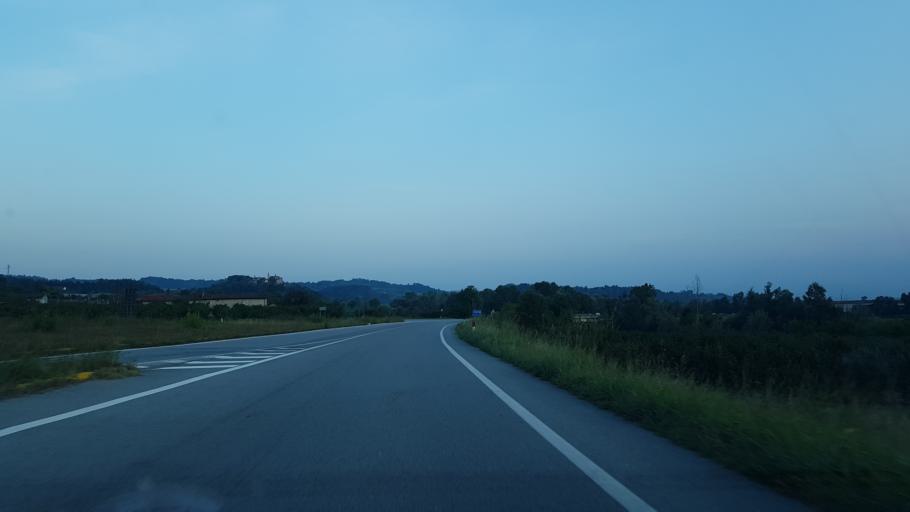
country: IT
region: Piedmont
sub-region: Provincia di Cuneo
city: Monchiero Borgonuovo
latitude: 44.5810
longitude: 7.9084
